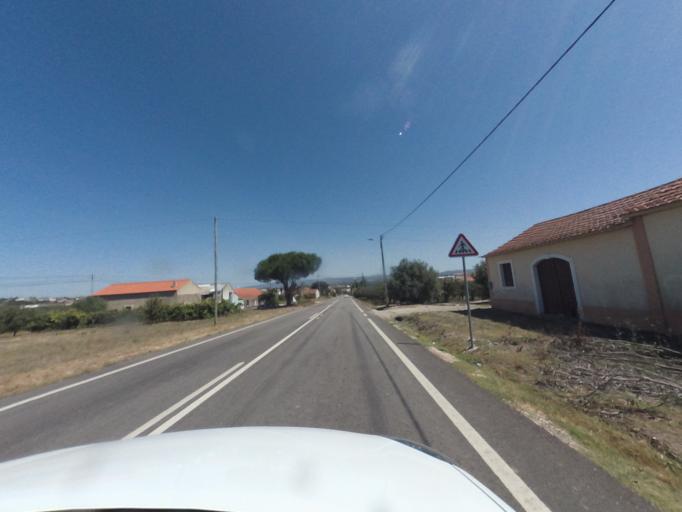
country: PT
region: Leiria
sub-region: Alcobaca
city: Alcobaca
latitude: 39.5200
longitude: -9.0234
